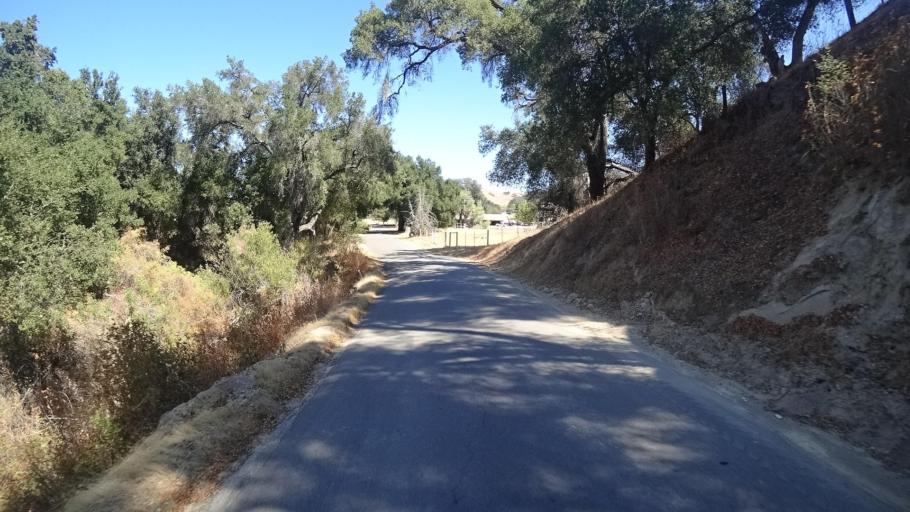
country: US
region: California
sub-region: San Luis Obispo County
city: Lake Nacimiento
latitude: 35.8360
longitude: -121.0416
